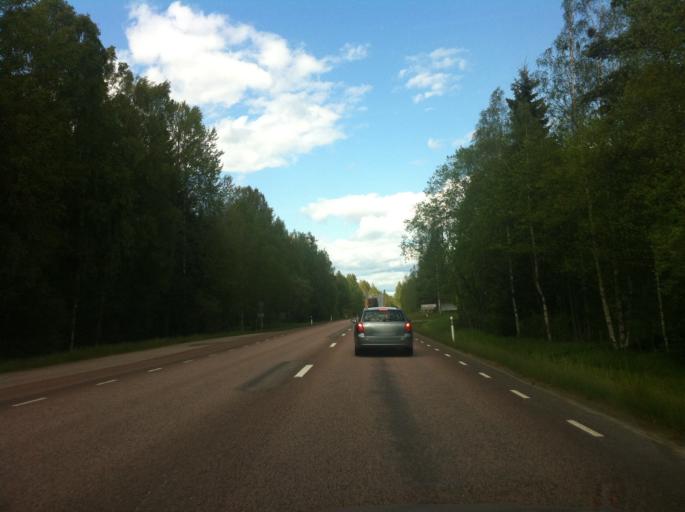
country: SE
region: Vaermland
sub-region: Kristinehamns Kommun
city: Kristinehamn
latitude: 59.3292
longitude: 14.1178
